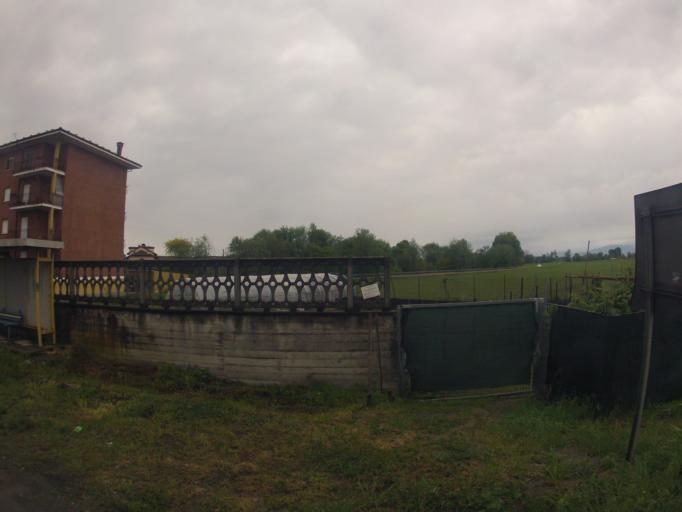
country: IT
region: Piedmont
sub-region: Provincia di Cuneo
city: Polonghera
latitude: 44.8024
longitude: 7.5969
